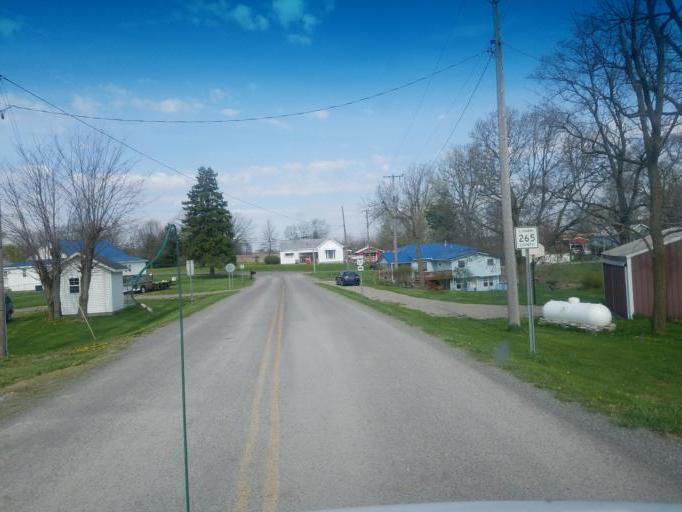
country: US
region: Ohio
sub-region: Logan County
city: Northwood
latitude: 40.4951
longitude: -83.6350
